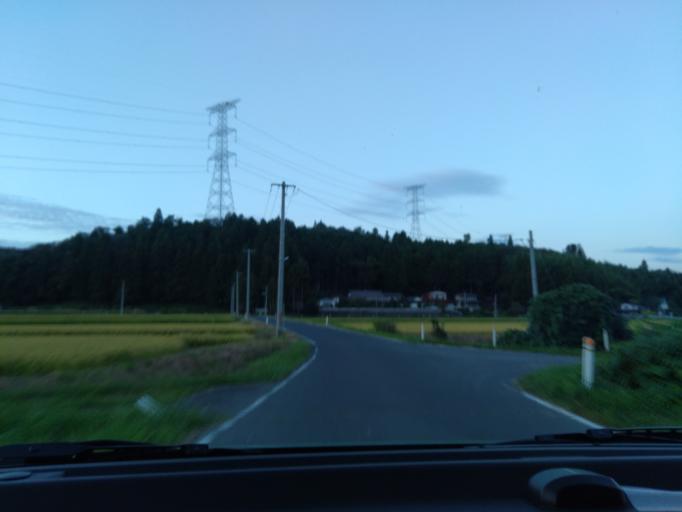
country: JP
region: Iwate
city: Ichinoseki
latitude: 38.8601
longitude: 141.1448
